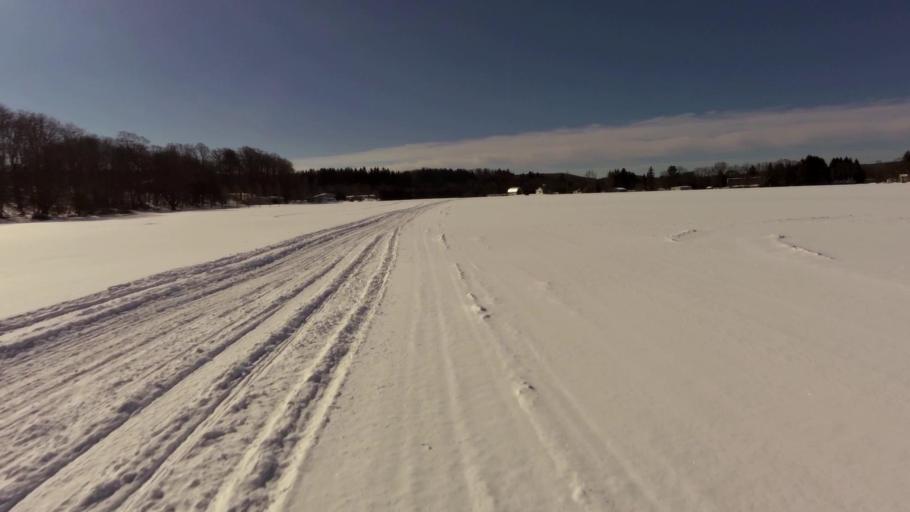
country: US
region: New York
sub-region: Cattaraugus County
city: Franklinville
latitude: 42.3477
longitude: -78.4481
